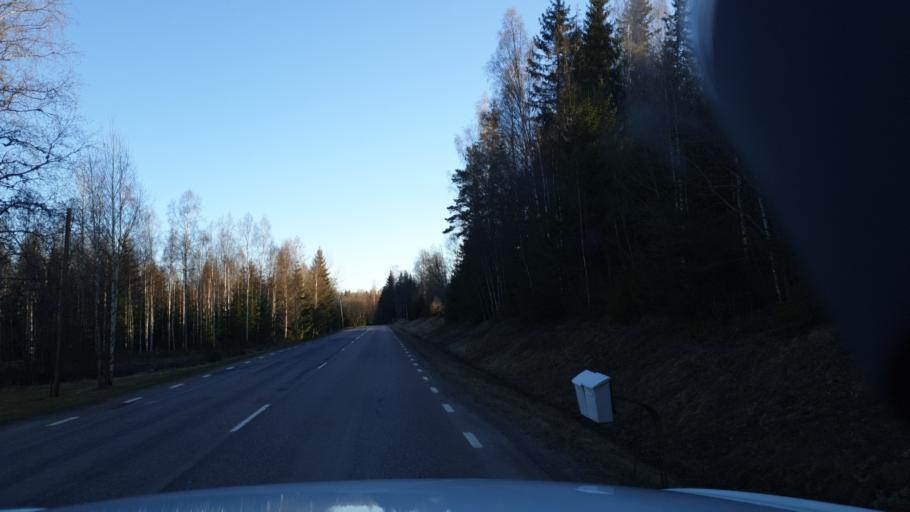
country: SE
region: Vaermland
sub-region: Eda Kommun
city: Charlottenberg
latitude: 59.8995
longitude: 12.3006
